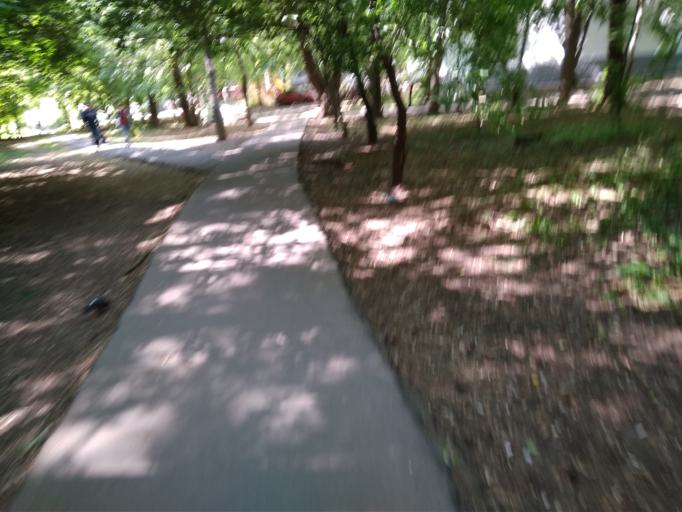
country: RU
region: Moskovskaya
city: Troitsk
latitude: 55.4858
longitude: 37.3012
